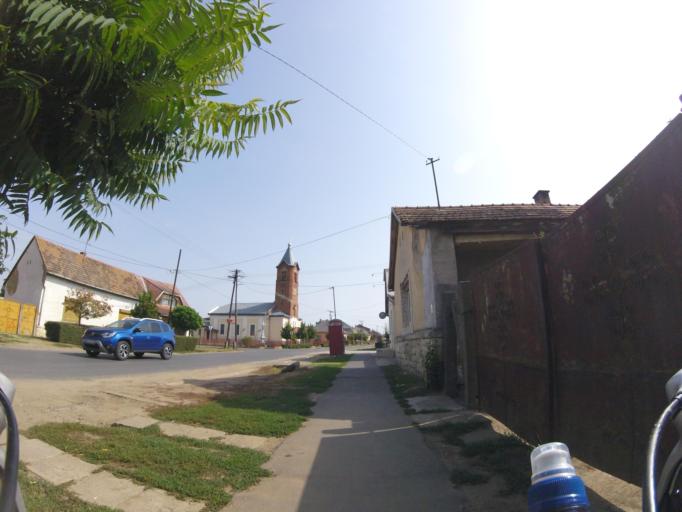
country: HU
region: Szabolcs-Szatmar-Bereg
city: Nyirmada
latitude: 48.0694
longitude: 22.1936
